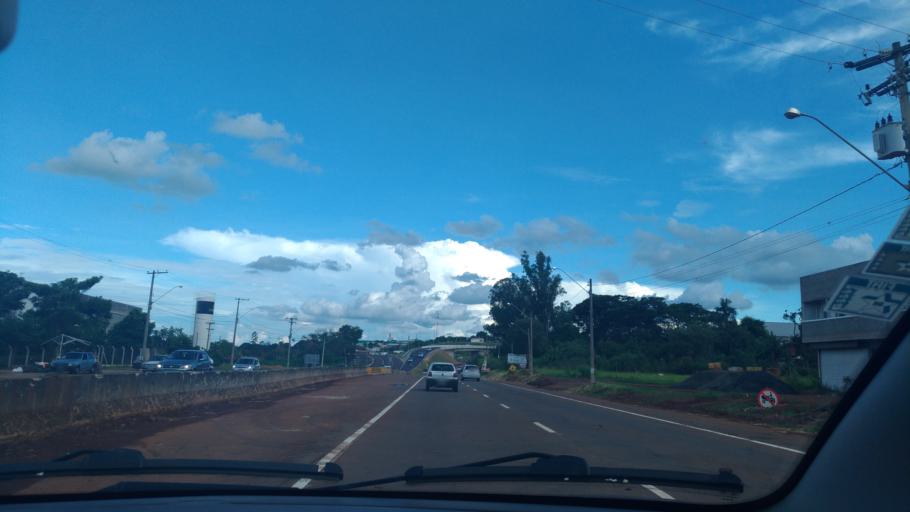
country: BR
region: Sao Paulo
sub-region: Nova Odessa
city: Nova Odessa
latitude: -22.7644
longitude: -47.3186
